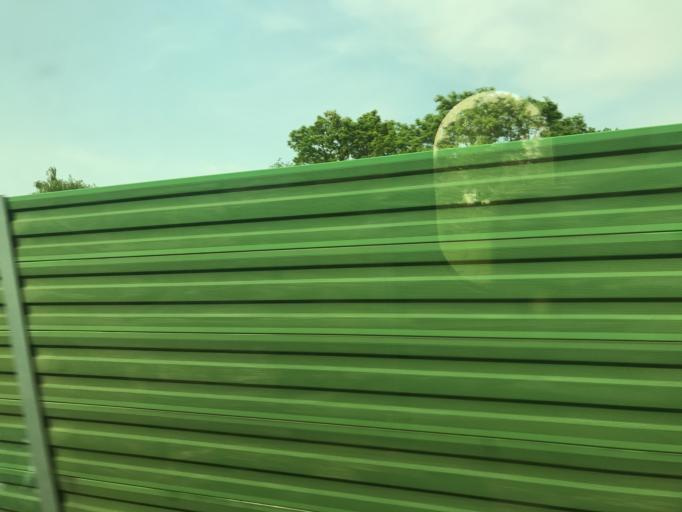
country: DE
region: Brandenburg
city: Pawesin
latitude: 52.5839
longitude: 12.7658
